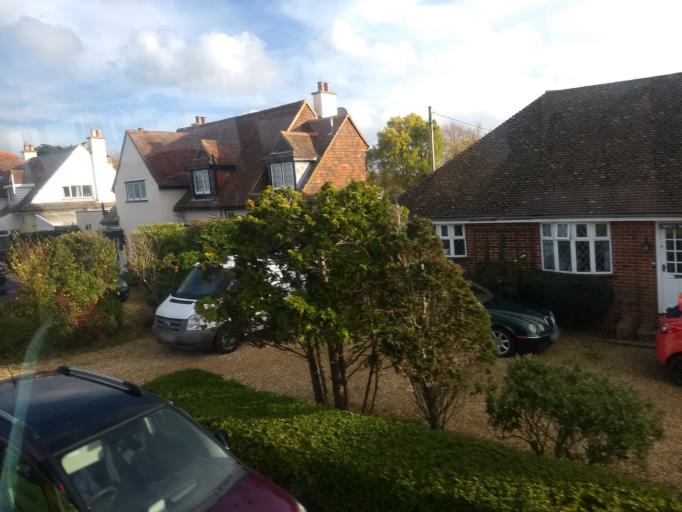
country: GB
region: England
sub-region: Isle of Wight
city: Yarmouth
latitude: 50.7069
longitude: -1.4840
